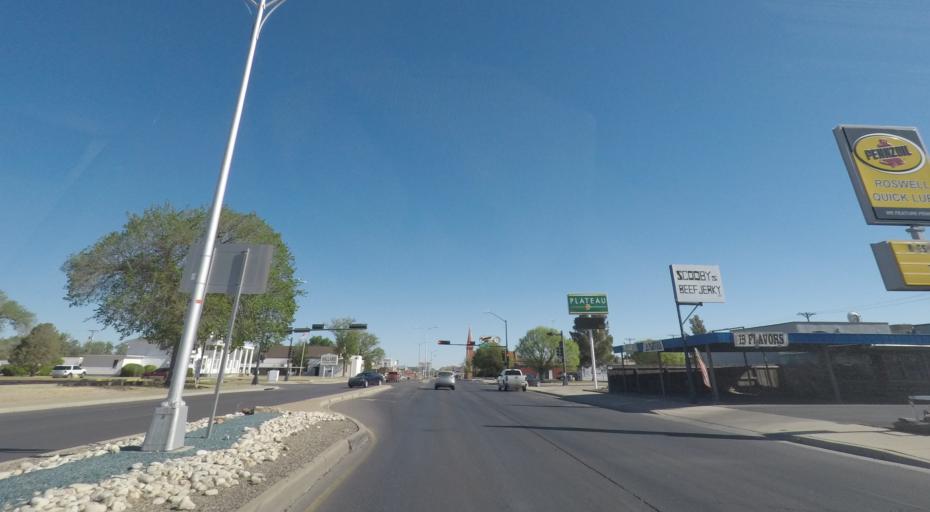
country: US
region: New Mexico
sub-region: Chaves County
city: Roswell
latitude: 33.3830
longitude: -104.5227
